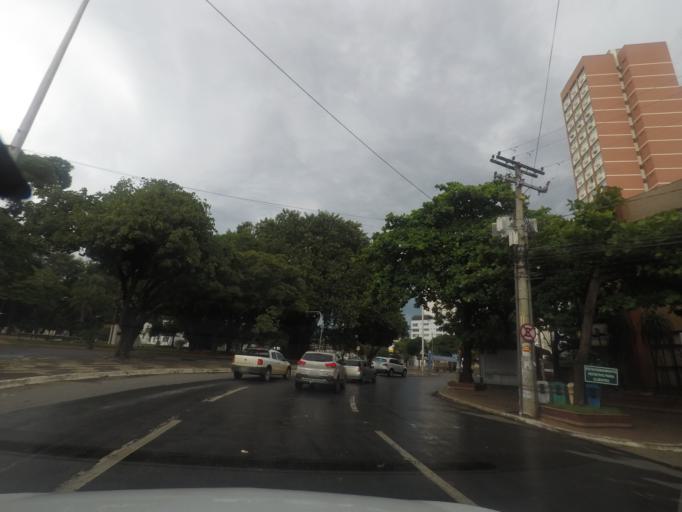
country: BR
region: Goias
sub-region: Goiania
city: Goiania
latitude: -16.6798
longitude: -49.2574
